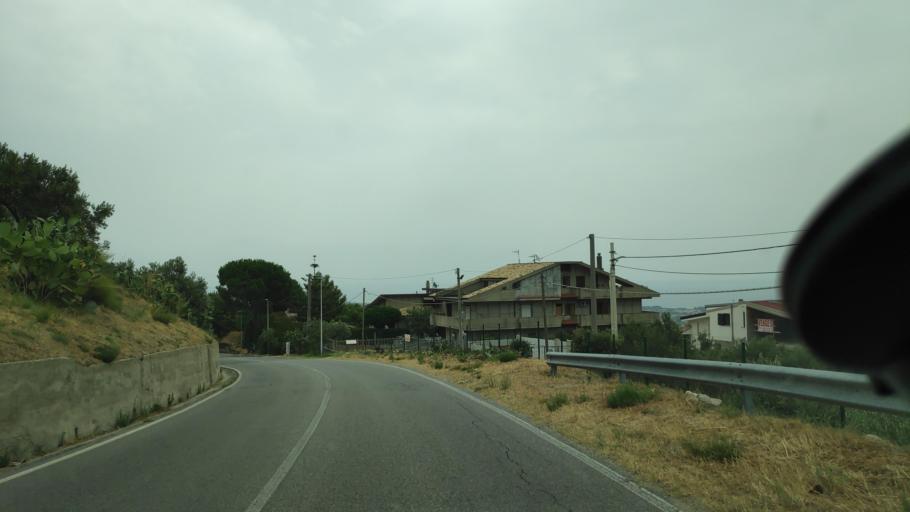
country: IT
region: Calabria
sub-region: Provincia di Catanzaro
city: Davoli
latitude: 38.6628
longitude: 16.5053
